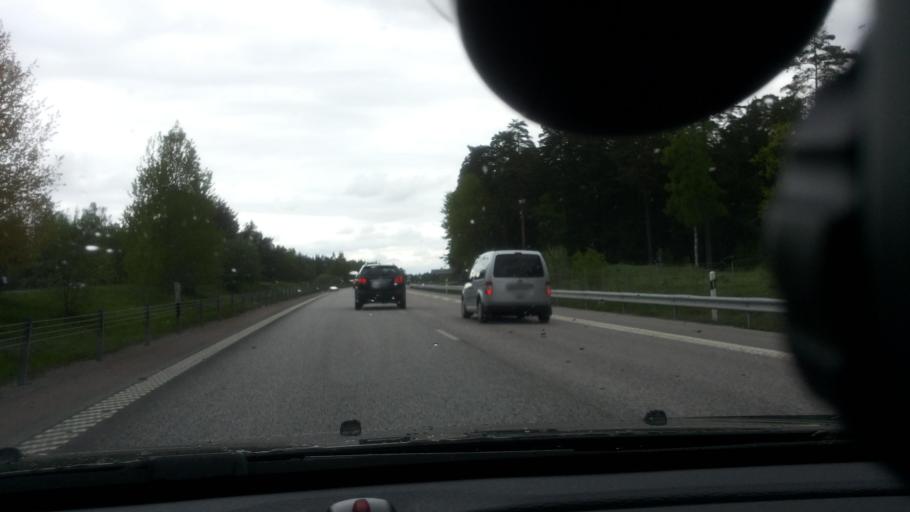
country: SE
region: Uppsala
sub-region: Uppsala Kommun
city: Alsike
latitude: 59.7886
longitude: 17.7764
